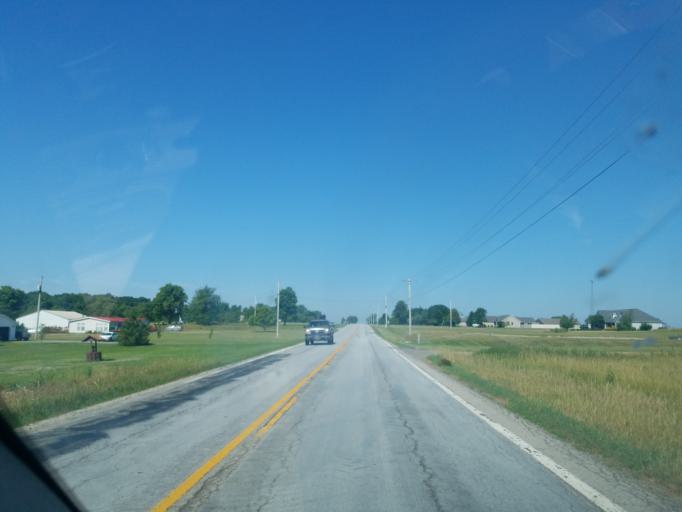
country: US
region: Ohio
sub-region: Logan County
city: Northwood
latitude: 40.4379
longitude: -83.7845
